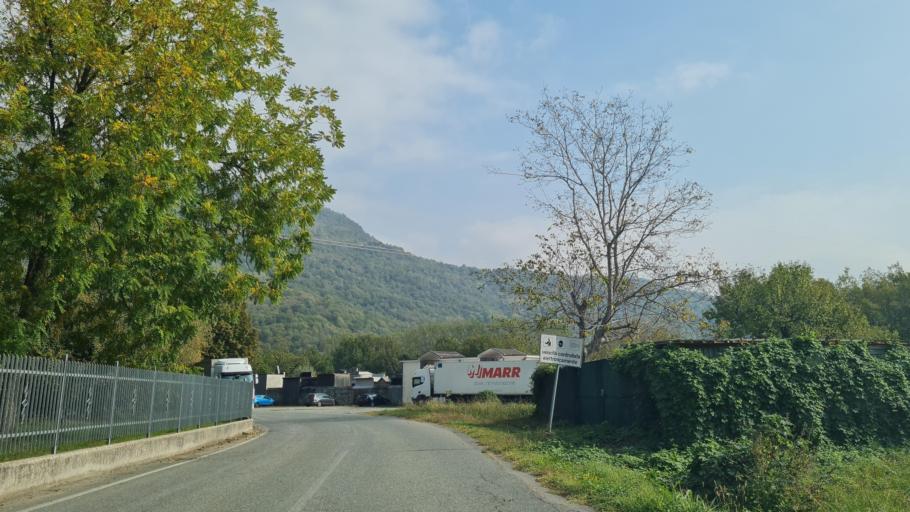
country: IT
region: Piedmont
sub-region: Provincia di Torino
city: Caprie
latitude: 45.1153
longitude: 7.3503
